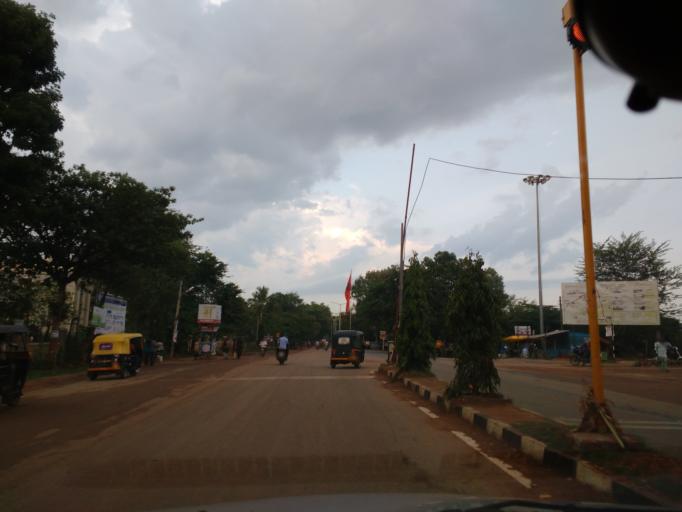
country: IN
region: Karnataka
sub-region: Tumkur
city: Tiptur
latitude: 13.2626
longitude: 76.4547
